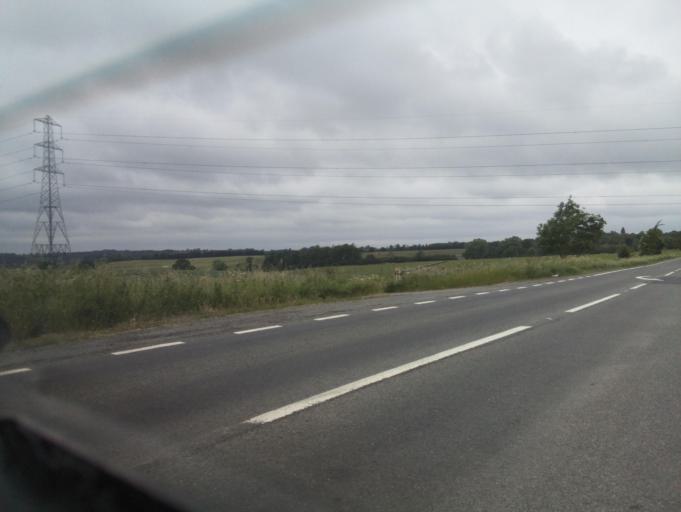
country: GB
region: England
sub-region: Leicestershire
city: Houghton on the Hill
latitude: 52.6130
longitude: -0.8924
